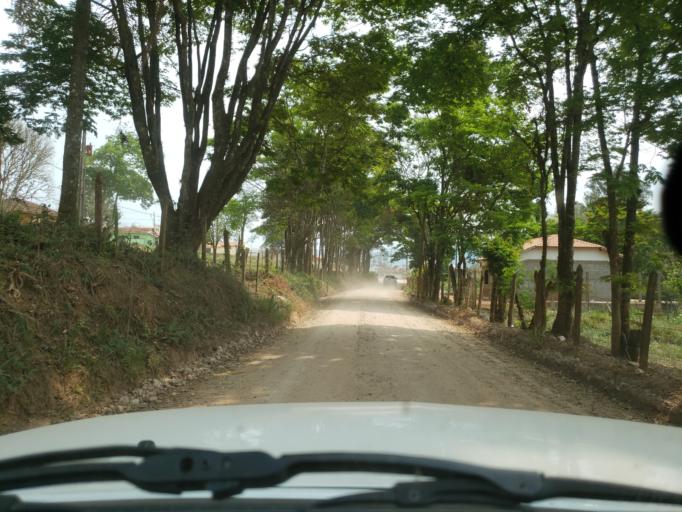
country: BR
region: Minas Gerais
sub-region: Jacutinga
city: Jacutinga
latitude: -22.3049
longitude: -46.6086
